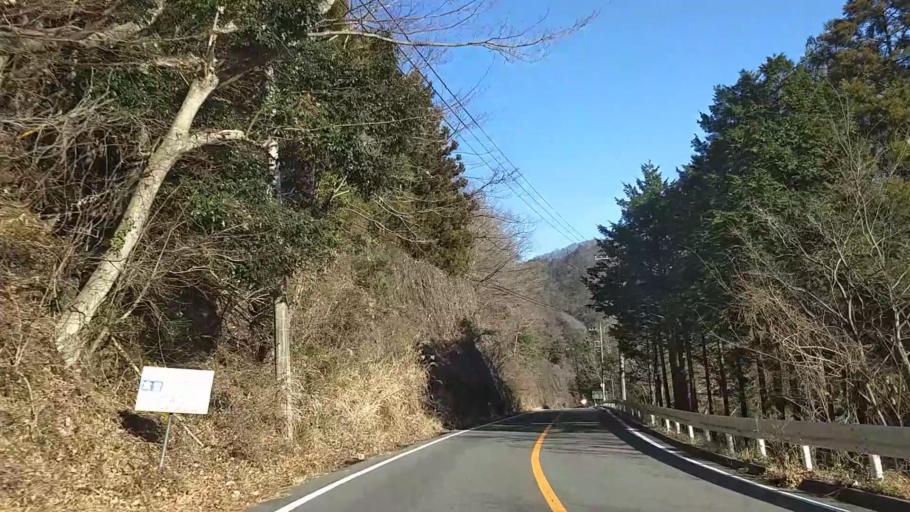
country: JP
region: Yamanashi
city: Uenohara
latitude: 35.5336
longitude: 139.1060
